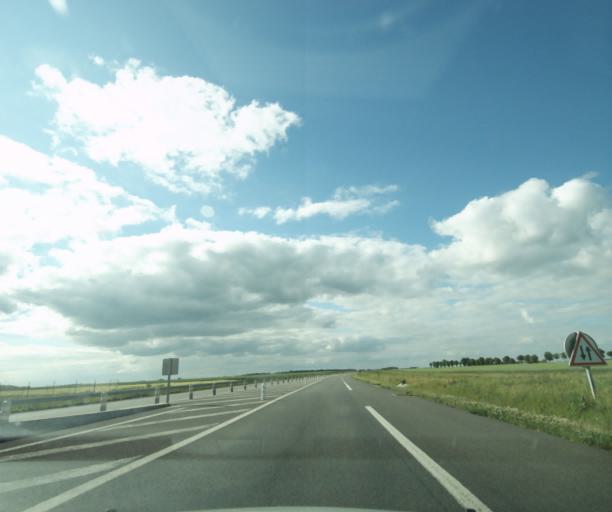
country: FR
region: Centre
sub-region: Departement d'Eure-et-Loir
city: Sours
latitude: 48.3733
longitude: 1.5889
